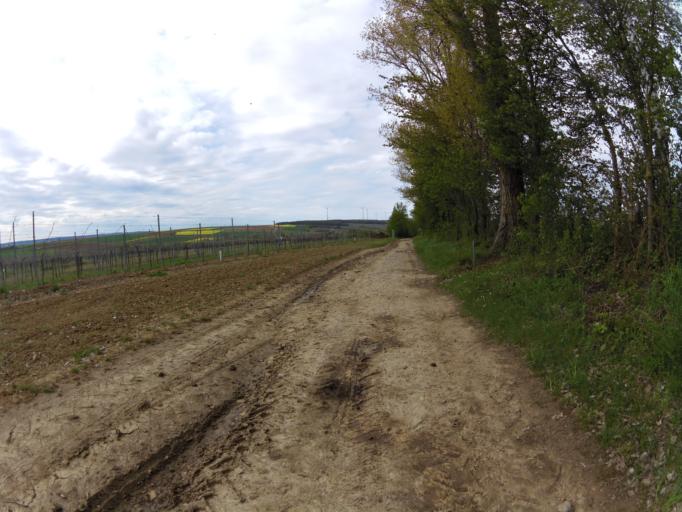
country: DE
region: Bavaria
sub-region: Regierungsbezirk Unterfranken
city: Prosselsheim
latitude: 49.8645
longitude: 10.1573
